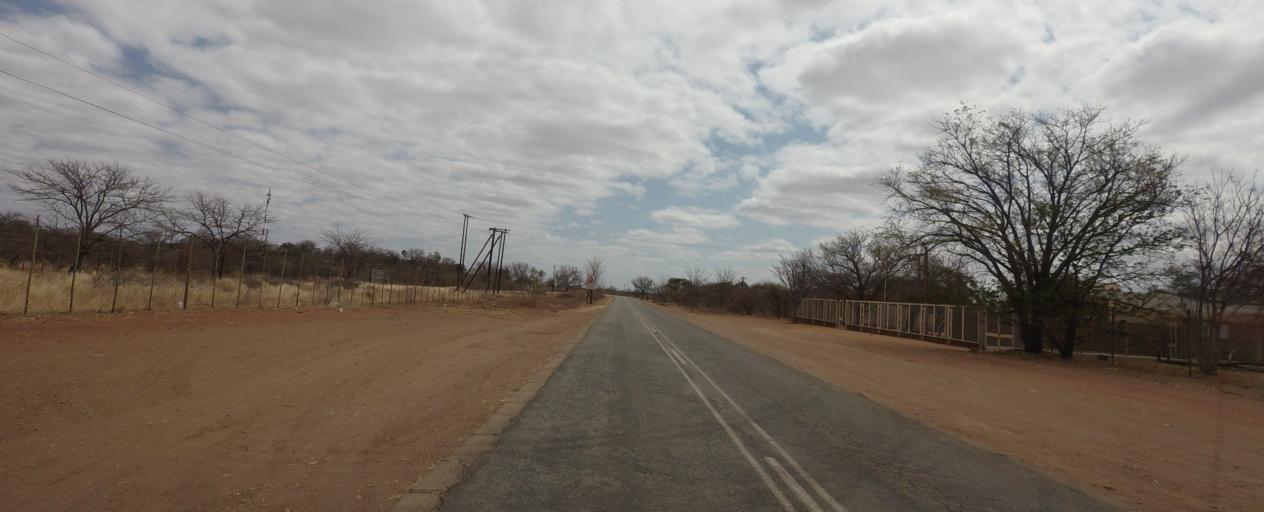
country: BW
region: Central
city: Makobeng
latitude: -23.0699
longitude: 27.9994
